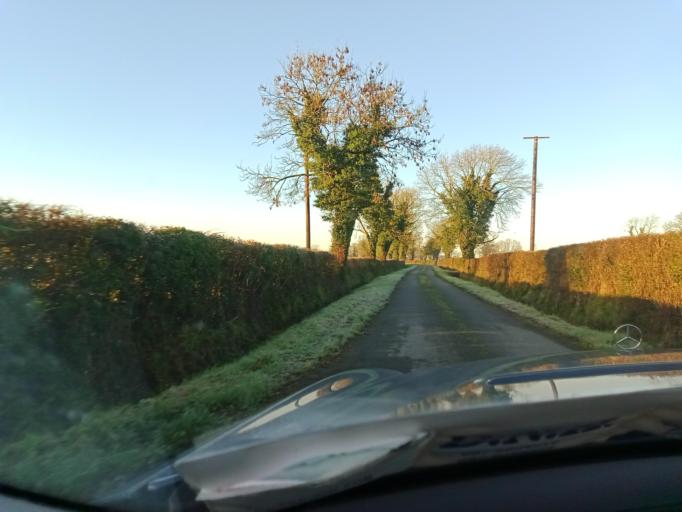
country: IE
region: Leinster
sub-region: Kilkenny
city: Callan
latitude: 52.5276
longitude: -7.4615
